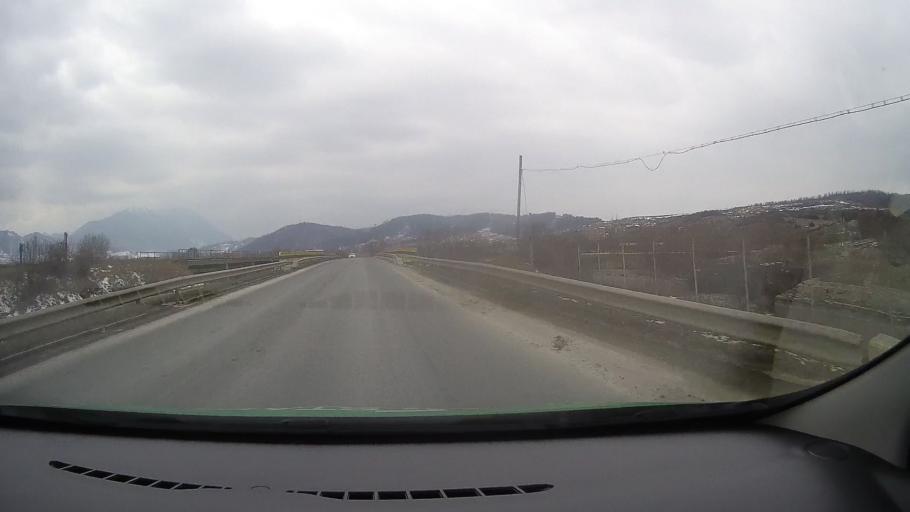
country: RO
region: Brasov
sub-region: Comuna Zarnesti
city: Tohanu Nou
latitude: 45.5773
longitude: 25.3923
